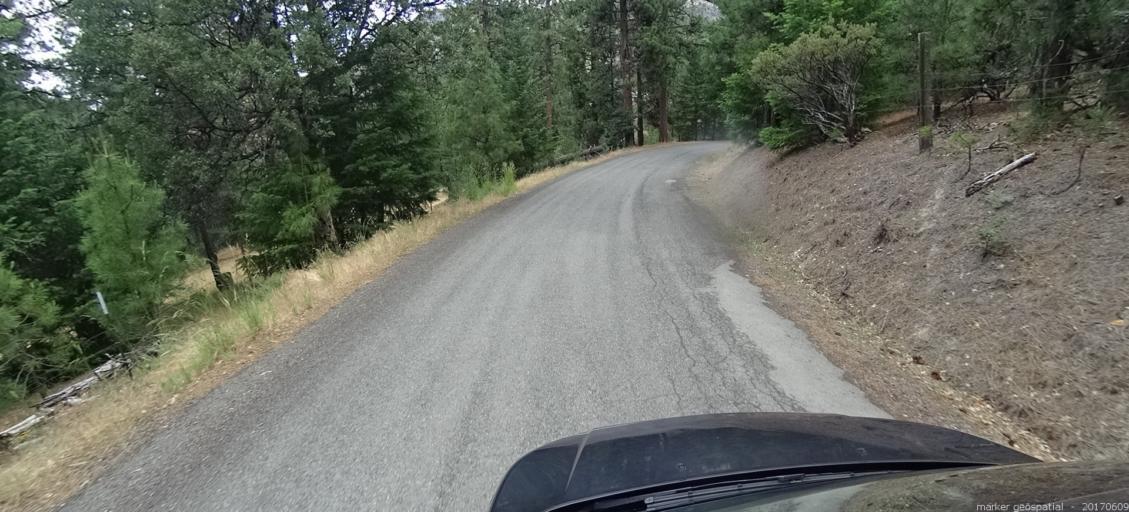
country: US
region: California
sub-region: Siskiyou County
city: Weed
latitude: 41.3018
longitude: -122.7989
